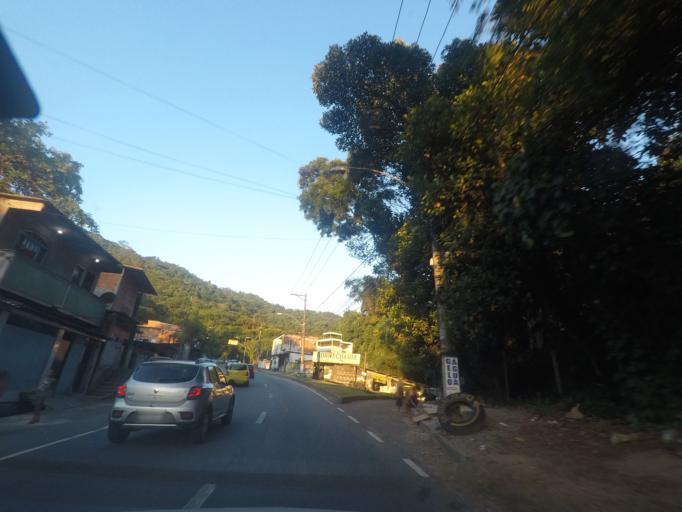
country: BR
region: Rio de Janeiro
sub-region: Rio De Janeiro
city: Rio de Janeiro
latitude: -22.9268
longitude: -43.3157
